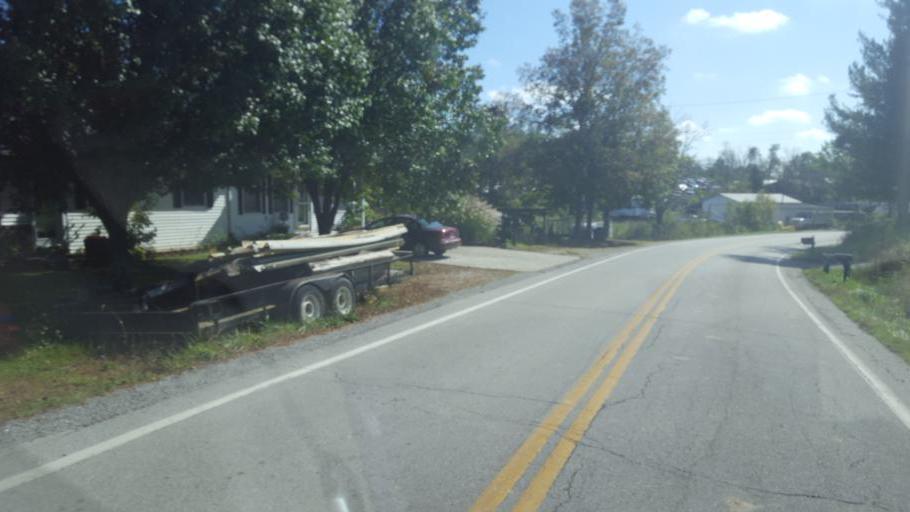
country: US
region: Kentucky
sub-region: Mason County
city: Maysville
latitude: 38.5783
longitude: -83.6472
